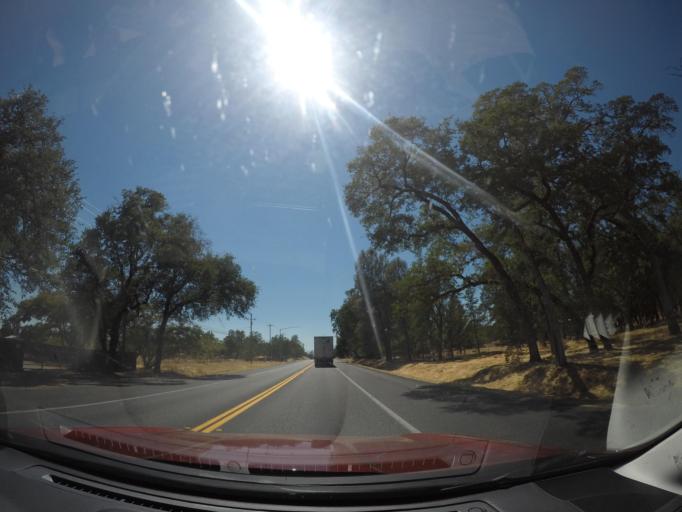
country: US
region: California
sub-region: Shasta County
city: Bella Vista
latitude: 40.6318
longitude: -122.2674
